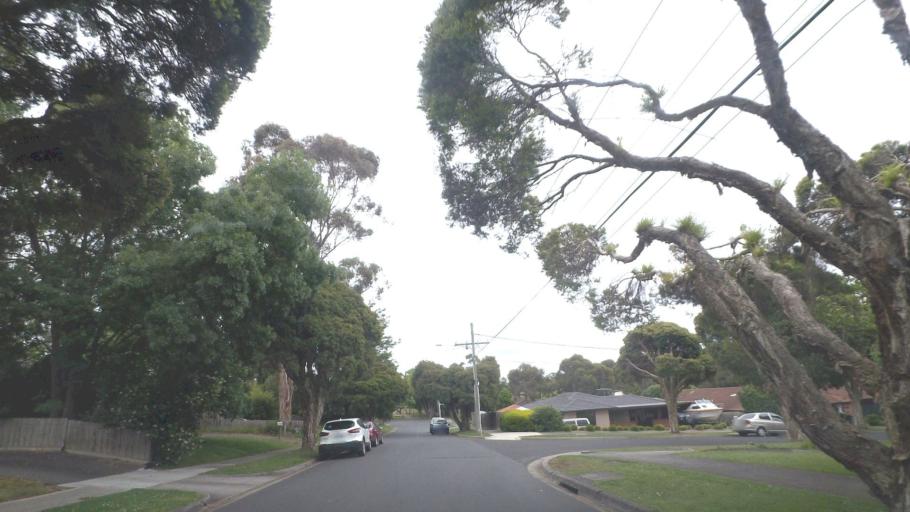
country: AU
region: Victoria
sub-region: Maroondah
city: Croydon South
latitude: -37.8135
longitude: 145.2823
